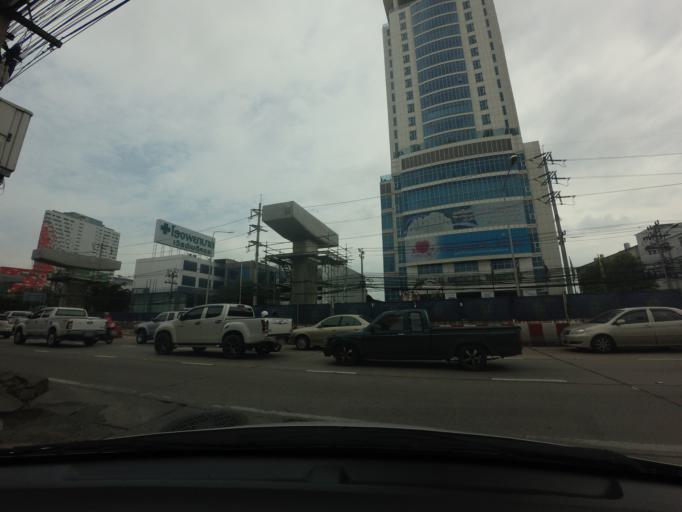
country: TH
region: Nonthaburi
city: Pak Kret
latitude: 13.9059
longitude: 100.5244
